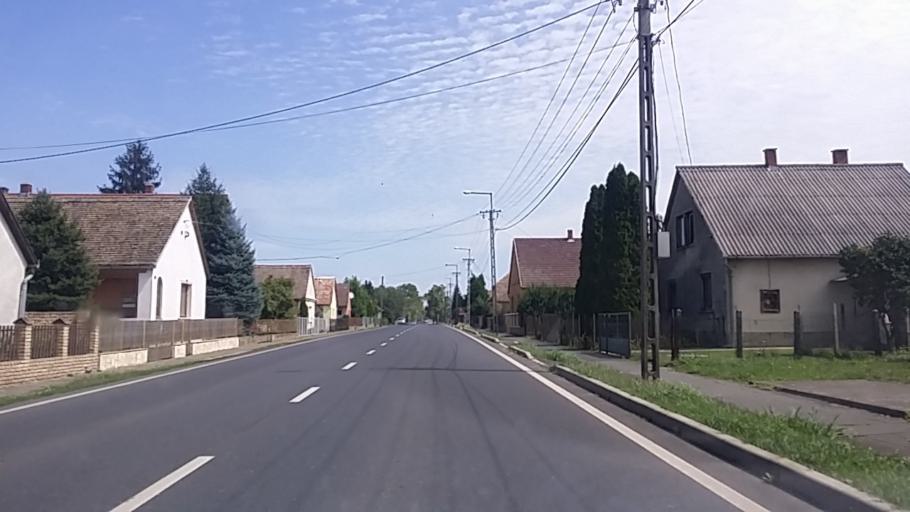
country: HU
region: Tolna
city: Dombovar
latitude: 46.3679
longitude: 18.0321
